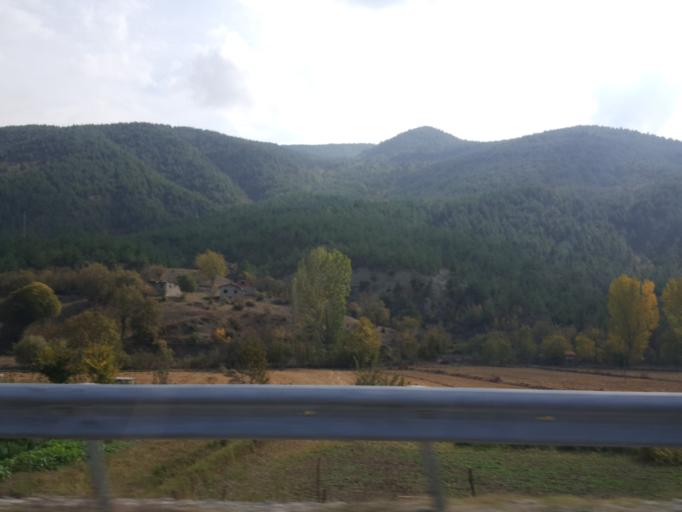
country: TR
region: Sinop
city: Sarayduzu
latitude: 41.3881
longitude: 34.9431
